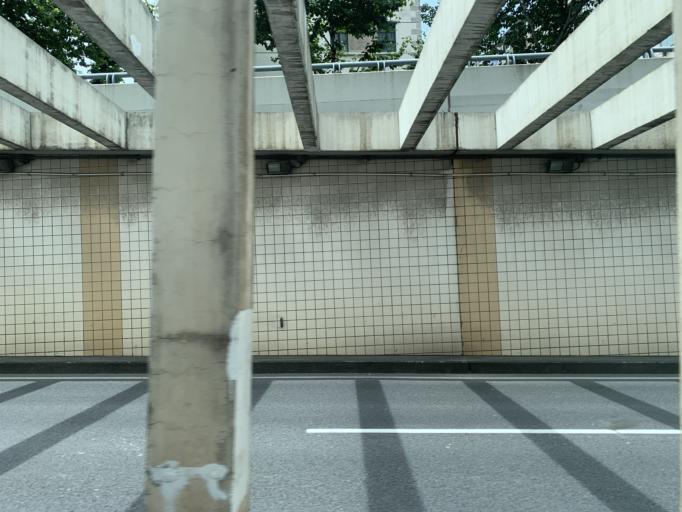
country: CN
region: Shanghai Shi
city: Pudong
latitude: 31.2282
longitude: 121.5124
